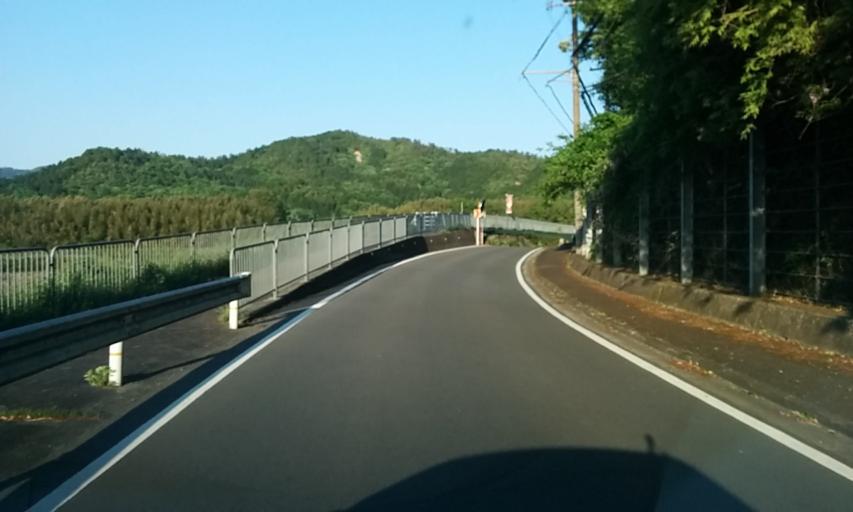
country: JP
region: Kyoto
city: Kameoka
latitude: 35.0926
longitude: 135.5078
